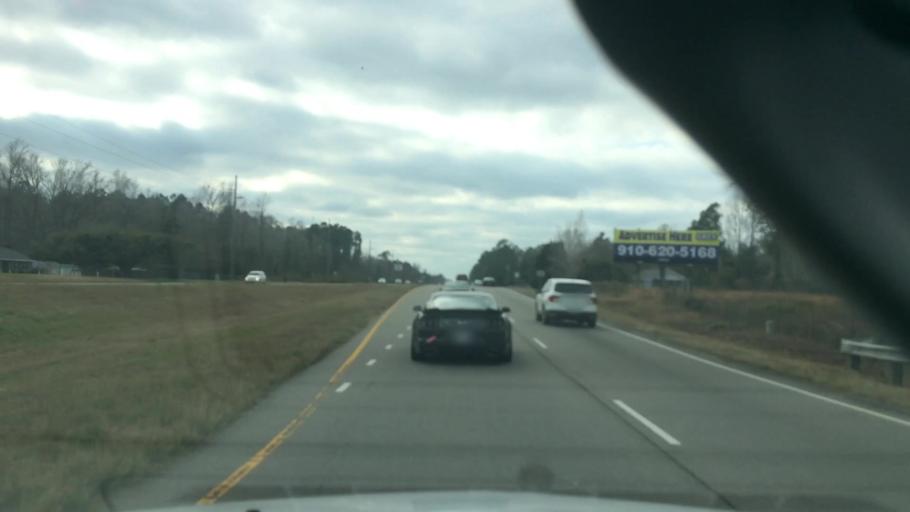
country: US
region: North Carolina
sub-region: Brunswick County
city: Shallotte
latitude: 34.0066
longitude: -78.3037
